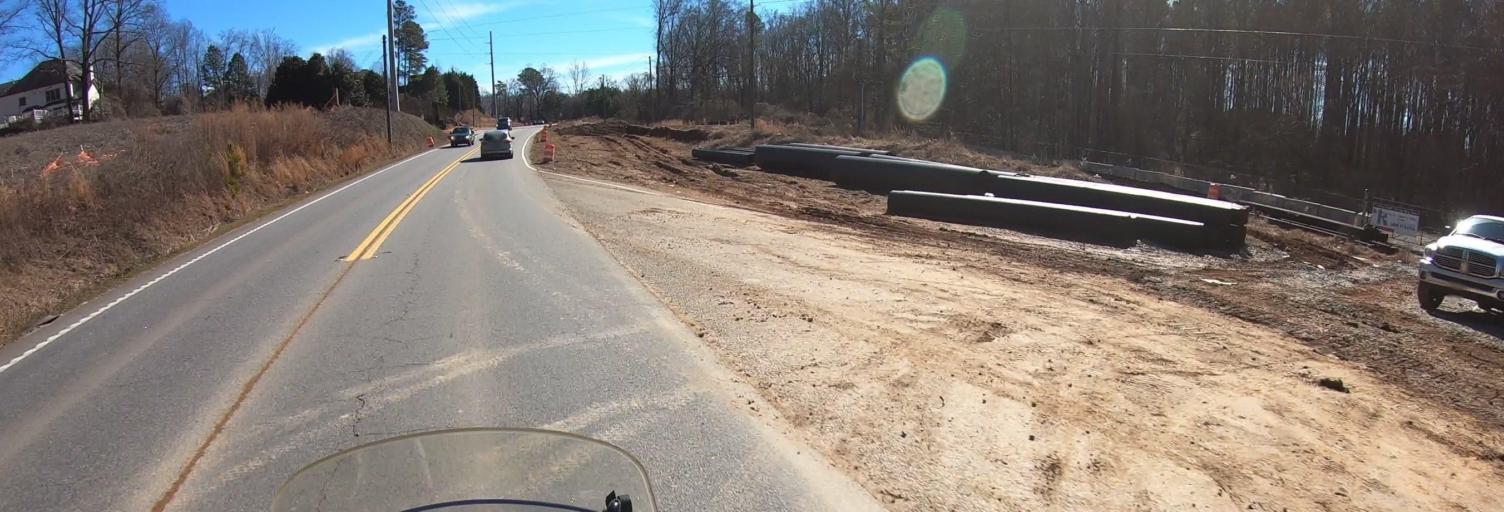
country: US
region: Georgia
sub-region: Forsyth County
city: Cumming
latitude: 34.2883
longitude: -84.1416
